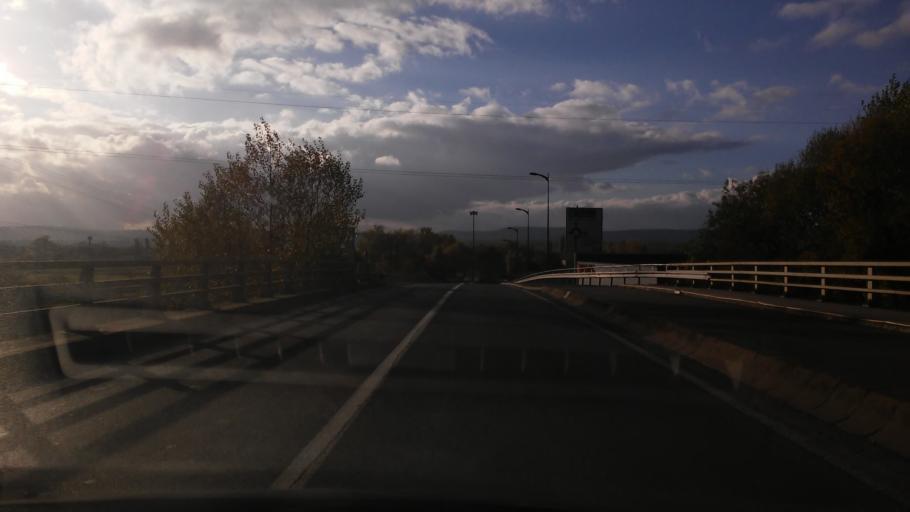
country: FR
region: Lorraine
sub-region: Departement de la Moselle
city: Talange
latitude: 49.2181
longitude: 6.1825
